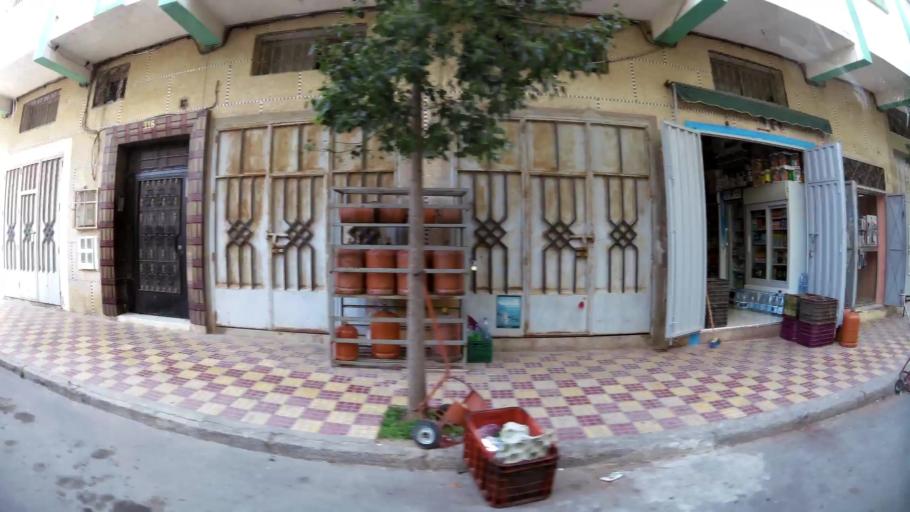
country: MA
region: Tanger-Tetouan
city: Tetouan
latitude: 35.5940
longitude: -5.3486
